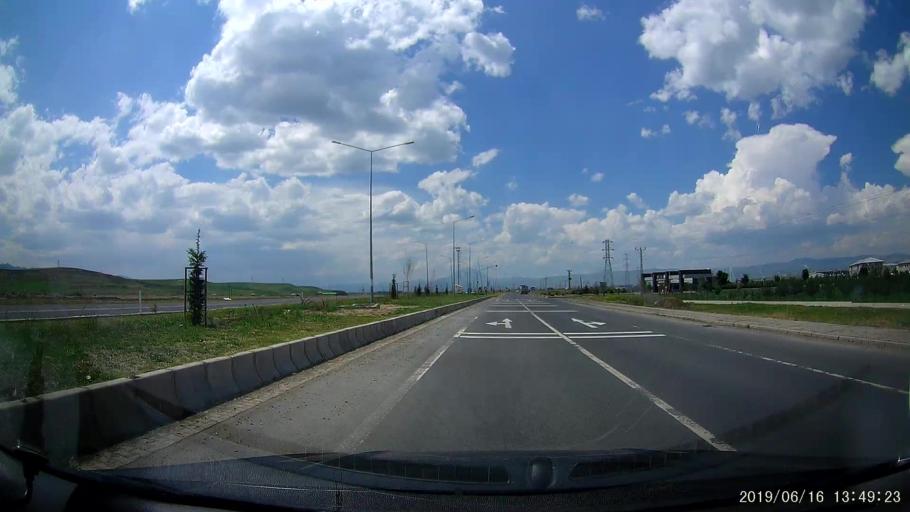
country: TR
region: Agri
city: Agri
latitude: 39.7168
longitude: 42.9915
